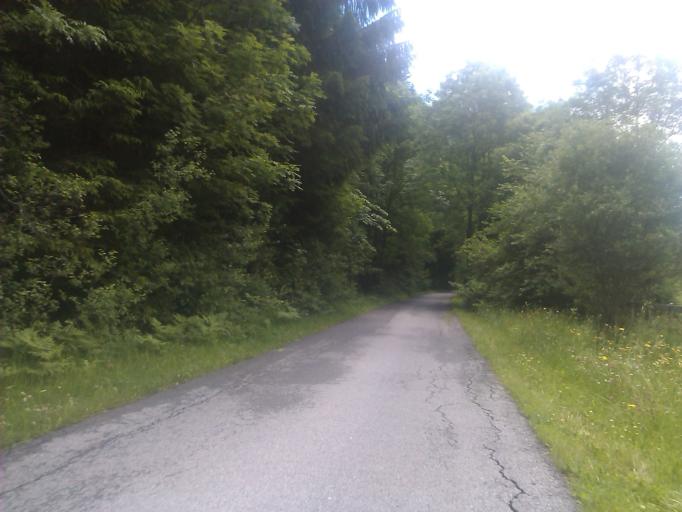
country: AT
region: Tyrol
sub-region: Politischer Bezirk Landeck
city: Fiss
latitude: 47.0334
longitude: 10.6312
